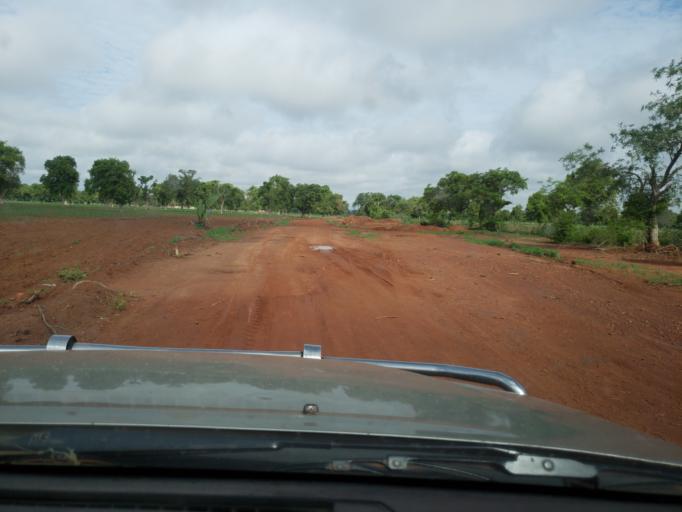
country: ML
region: Sikasso
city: Koutiala
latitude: 12.3924
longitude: -6.0089
